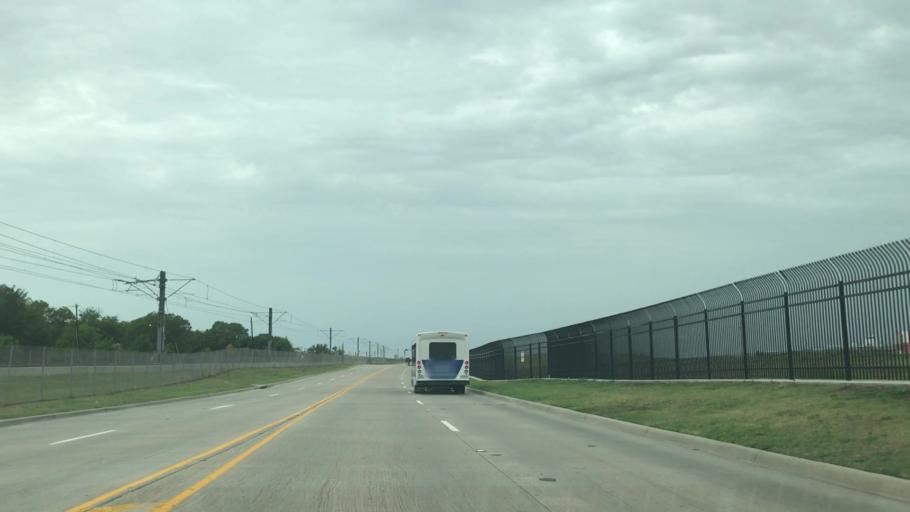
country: US
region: Texas
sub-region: Dallas County
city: University Park
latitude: 32.8344
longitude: -96.8463
